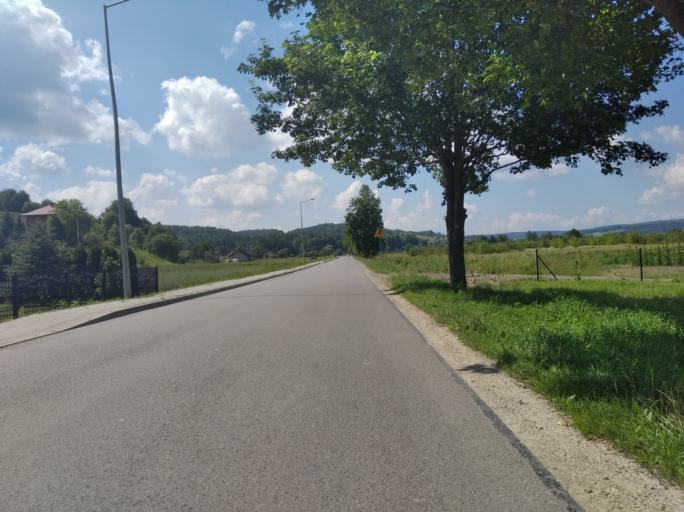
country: PL
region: Subcarpathian Voivodeship
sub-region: Powiat rzeszowski
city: Dynow
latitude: 49.7906
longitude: 22.2403
